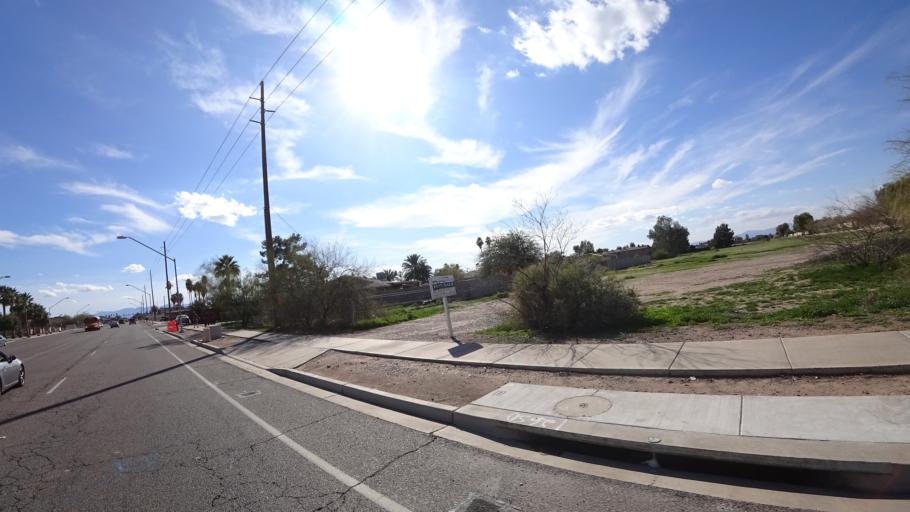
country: US
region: Arizona
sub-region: Maricopa County
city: Glendale
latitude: 33.5415
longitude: -112.2205
